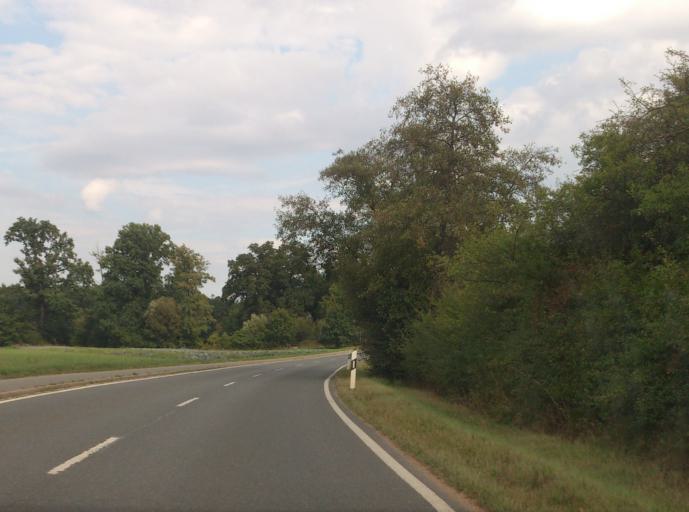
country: DE
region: Bavaria
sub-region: Regierungsbezirk Mittelfranken
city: Wetzendorf
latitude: 49.5226
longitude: 11.0562
